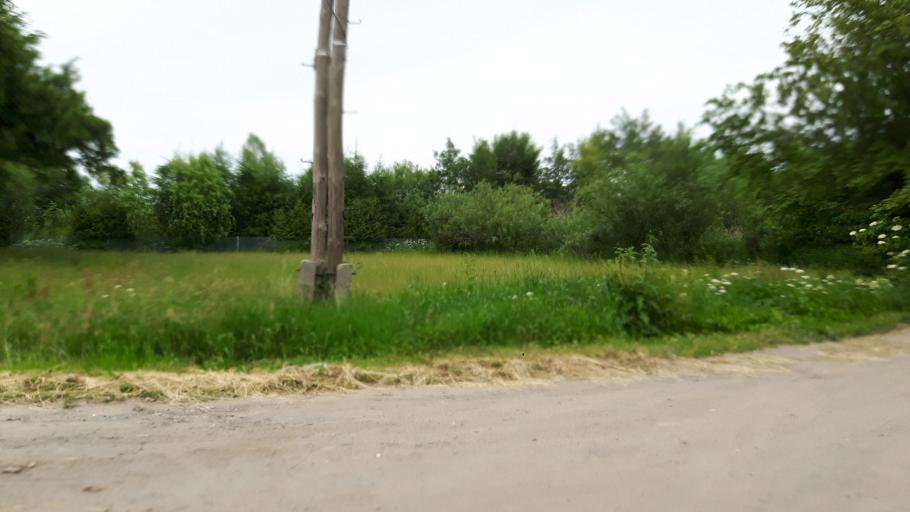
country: PL
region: Warmian-Masurian Voivodeship
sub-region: Powiat elblaski
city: Elblag
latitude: 54.2055
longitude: 19.3291
